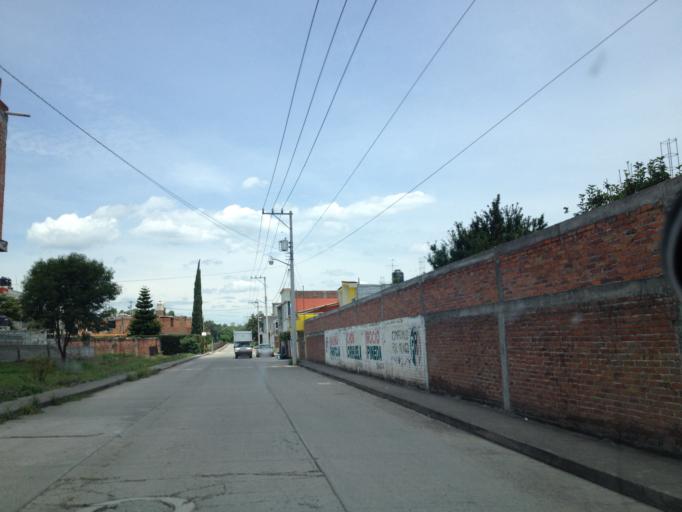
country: MX
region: Michoacan
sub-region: Tarimbaro
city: El Colegio
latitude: 19.7913
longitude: -101.1762
